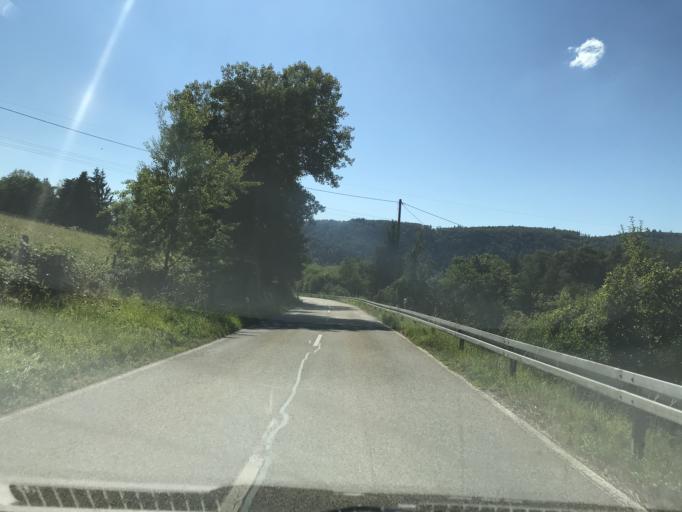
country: DE
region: Baden-Wuerttemberg
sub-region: Freiburg Region
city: Hausen
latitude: 47.6610
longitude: 7.8481
